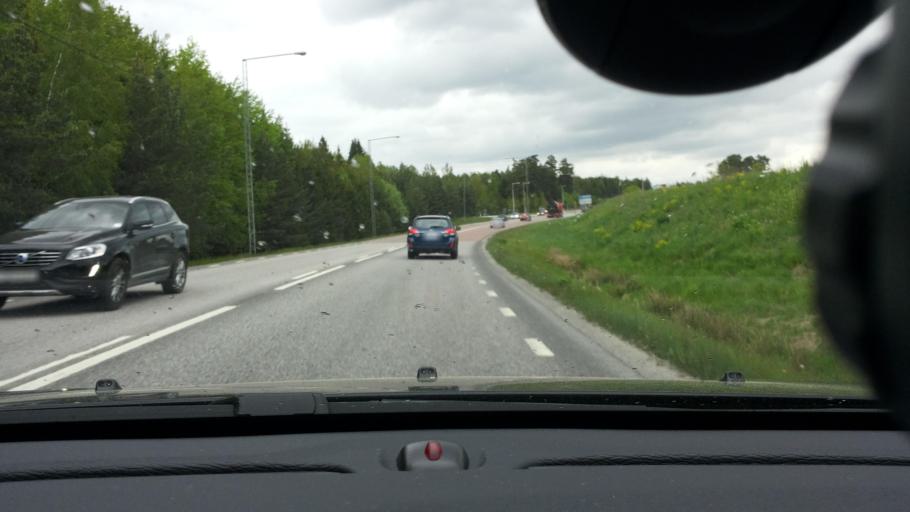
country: SE
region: Stockholm
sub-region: Taby Kommun
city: Taby
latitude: 59.4699
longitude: 18.1154
